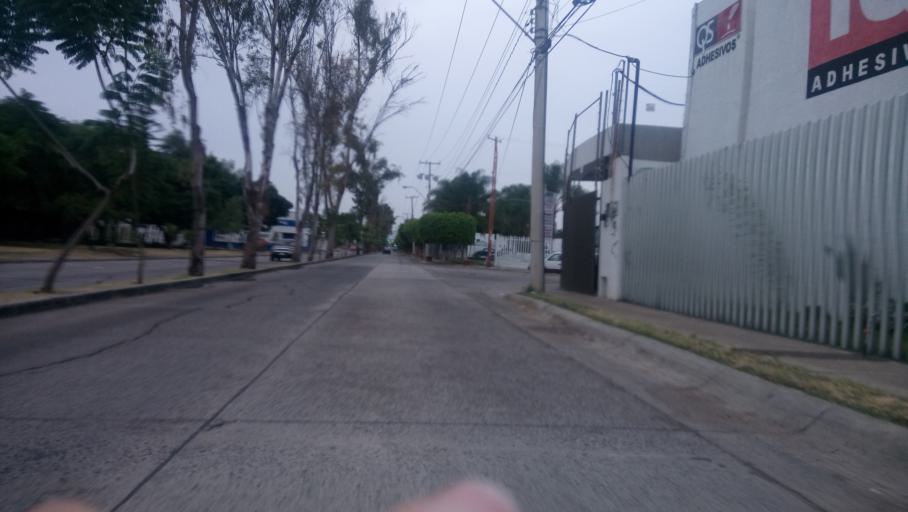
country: MX
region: Guanajuato
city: Leon
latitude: 21.1416
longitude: -101.6621
